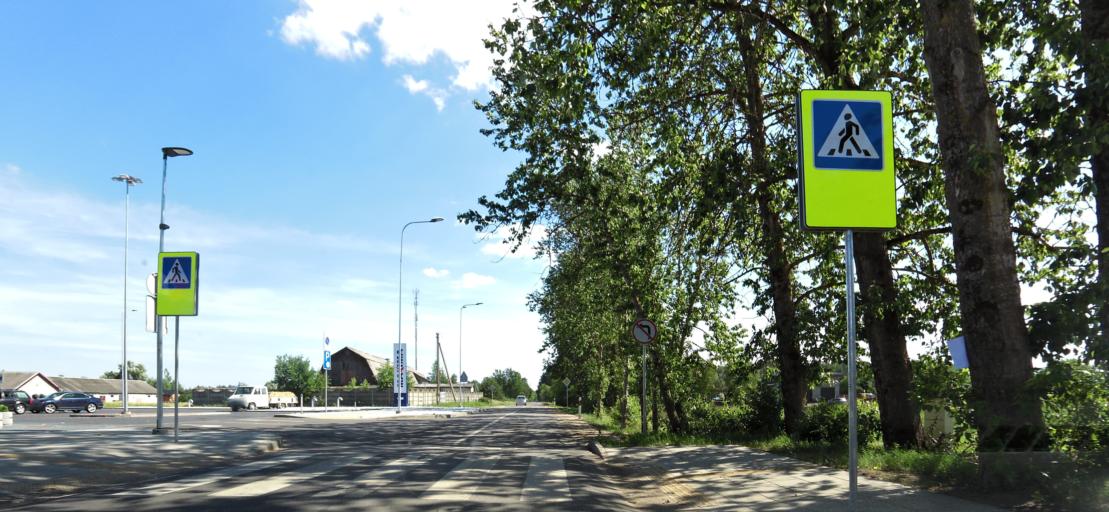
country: LT
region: Vilnius County
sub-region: Vilnius
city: Fabijoniskes
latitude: 54.8006
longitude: 25.3482
